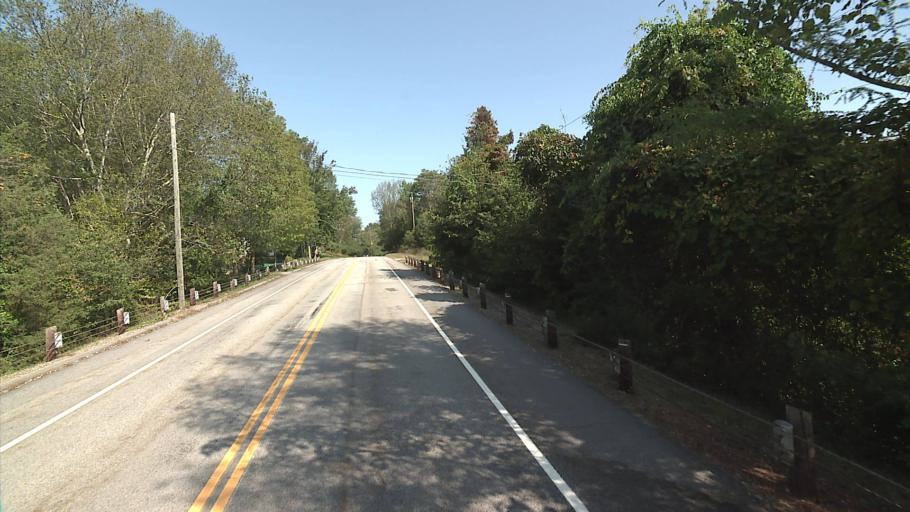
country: US
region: Connecticut
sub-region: Windham County
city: Wauregan
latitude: 41.7315
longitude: -71.9650
